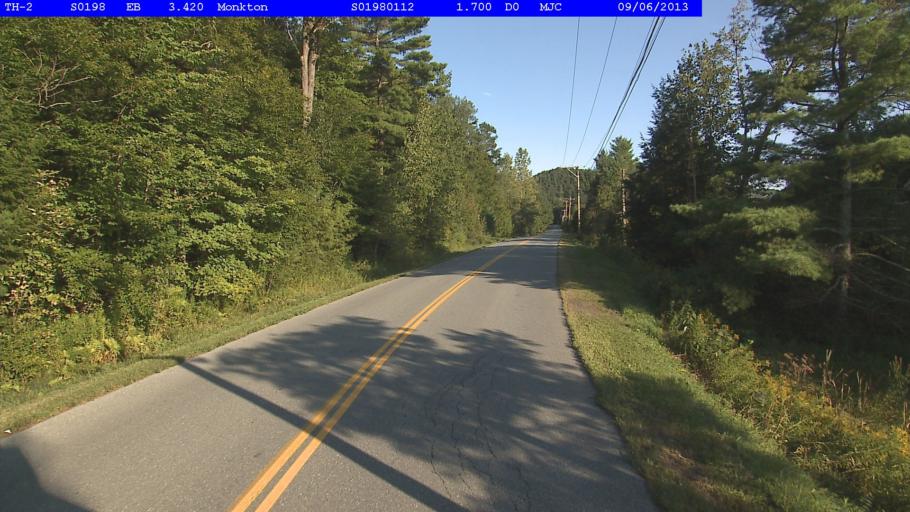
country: US
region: Vermont
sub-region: Chittenden County
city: Hinesburg
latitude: 44.2457
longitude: -73.1665
